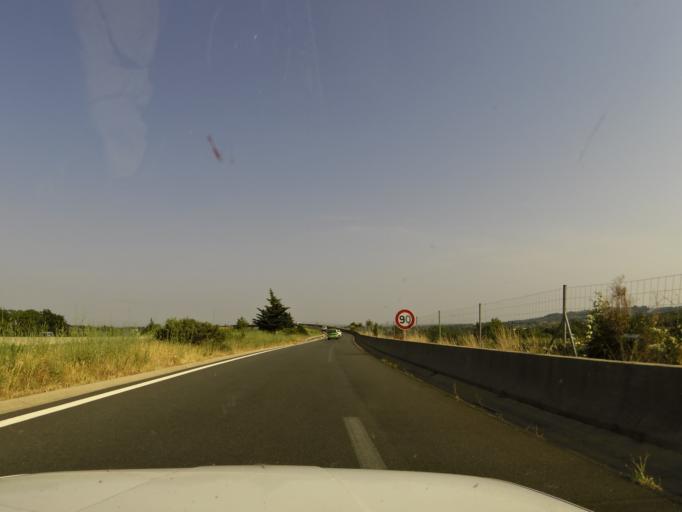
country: FR
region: Languedoc-Roussillon
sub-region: Departement de l'Herault
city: Nebian
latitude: 43.6575
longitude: 3.4449
